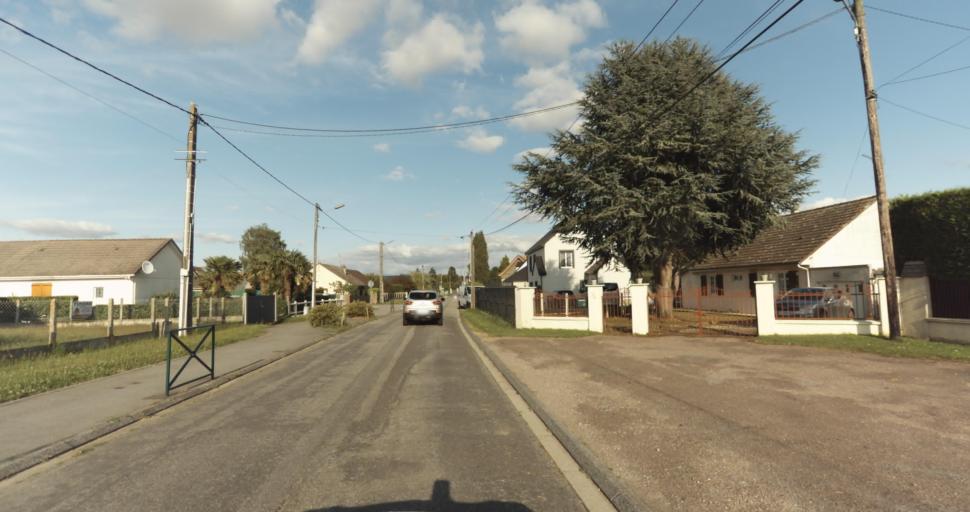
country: FR
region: Haute-Normandie
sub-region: Departement de l'Eure
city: Marcilly-sur-Eure
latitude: 48.9115
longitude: 1.2736
